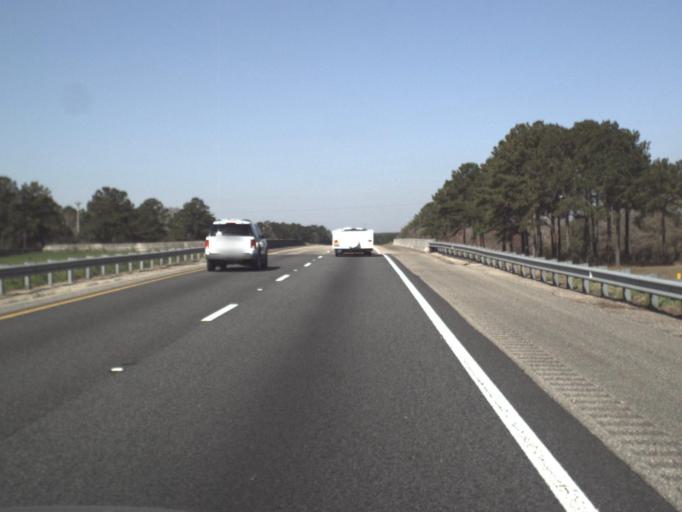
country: US
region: Florida
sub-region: Gadsden County
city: Gretna
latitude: 30.5781
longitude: -84.6989
